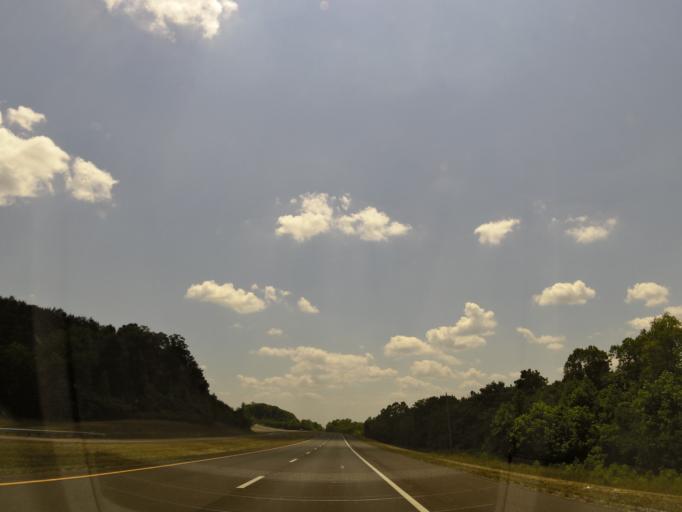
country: US
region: Tennessee
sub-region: Rhea County
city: Dayton
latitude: 35.5755
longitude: -84.9442
